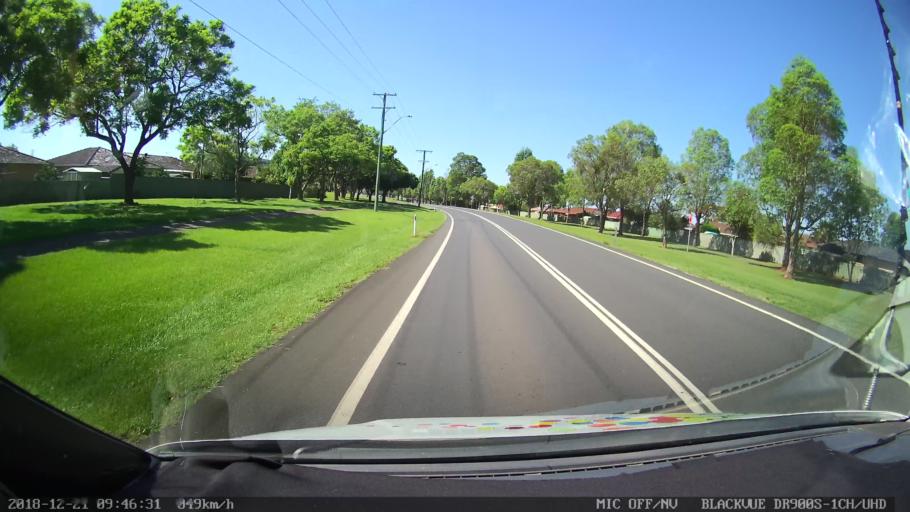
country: AU
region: New South Wales
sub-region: Clarence Valley
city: Grafton
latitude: -29.6390
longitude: 152.9260
